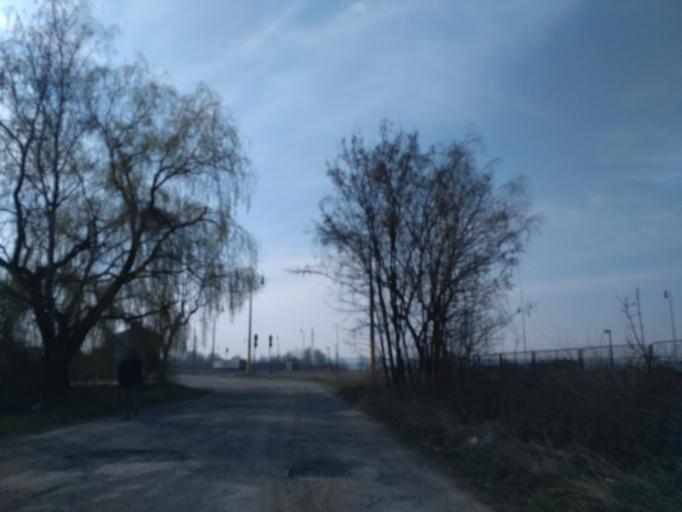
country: SK
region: Kosicky
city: Moldava nad Bodvou
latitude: 48.6012
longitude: 21.0035
